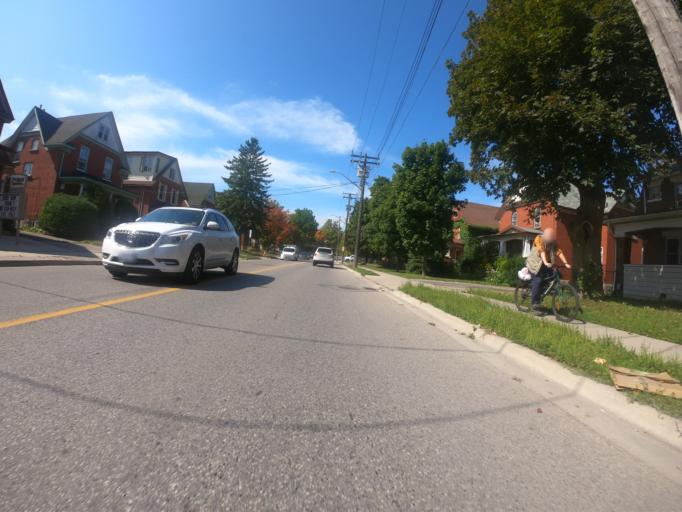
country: CA
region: Ontario
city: Waterloo
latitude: 43.4488
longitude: -80.5033
